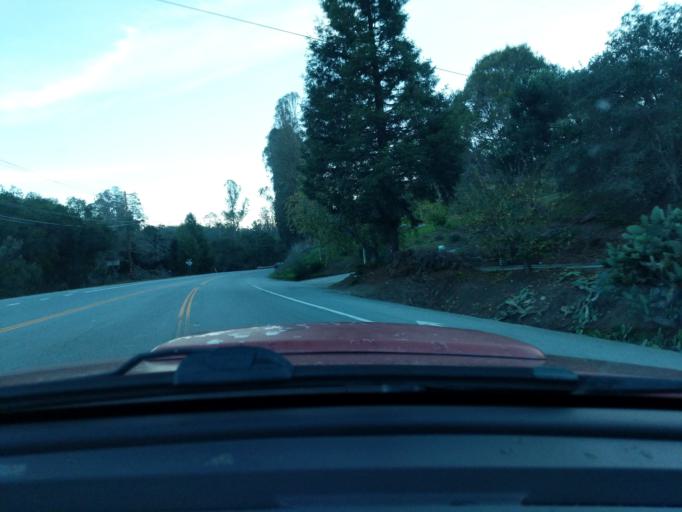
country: US
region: California
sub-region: Monterey County
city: Prunedale
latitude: 36.8216
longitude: -121.6734
